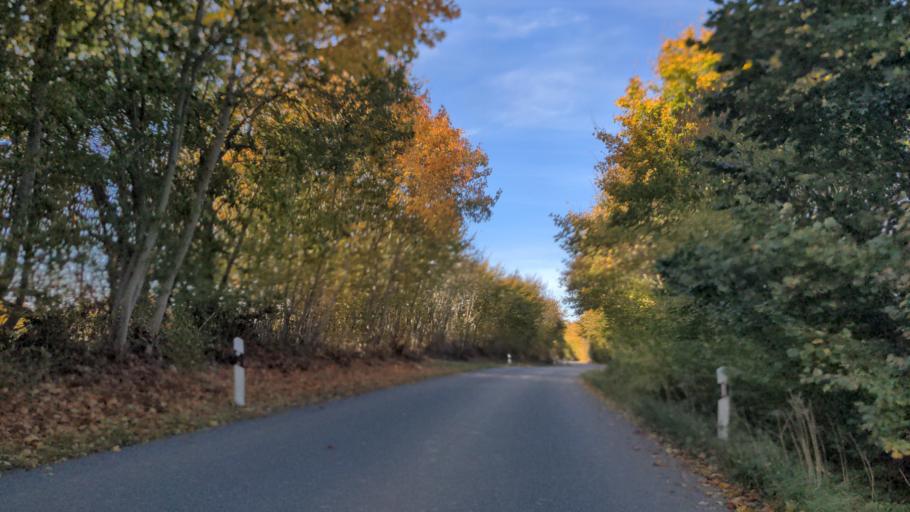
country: DE
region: Schleswig-Holstein
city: Kirchnuchel
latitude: 54.1658
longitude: 10.6693
